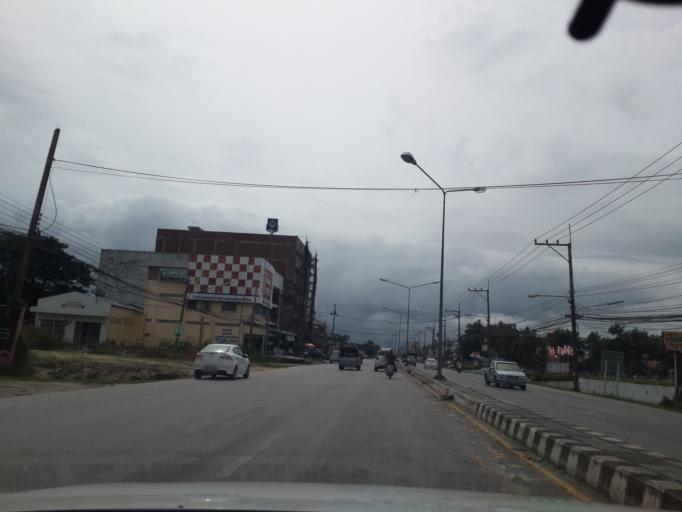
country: TH
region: Pattani
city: Pattani
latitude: 6.8633
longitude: 101.2371
